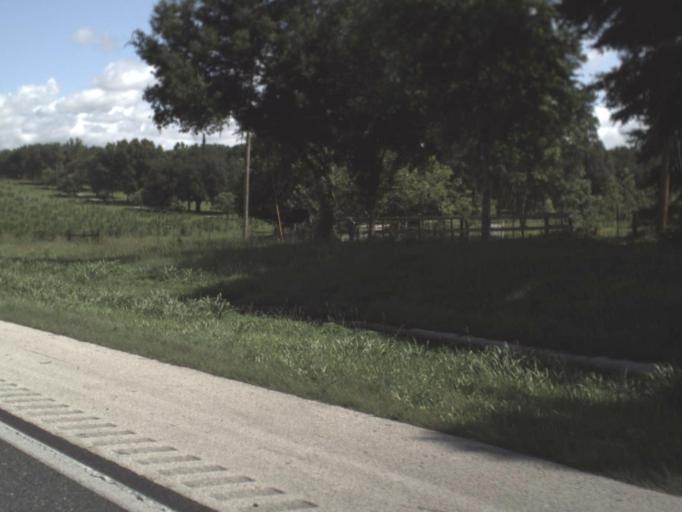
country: US
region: Florida
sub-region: Alachua County
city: Alachua
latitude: 29.6959
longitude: -82.4530
